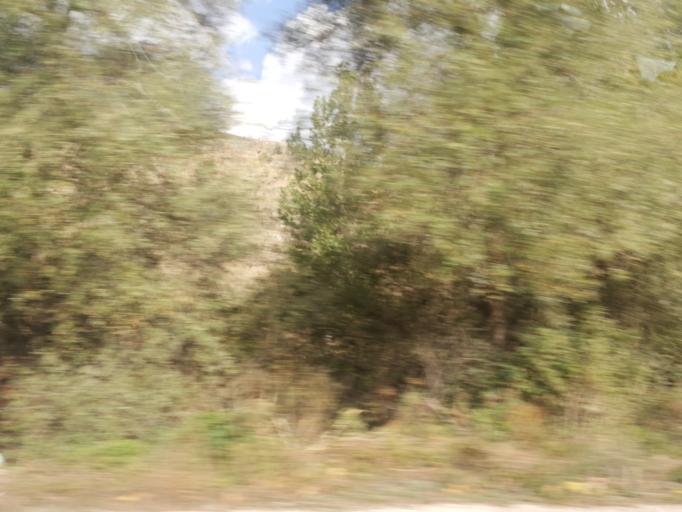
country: TR
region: Tokat
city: Artova
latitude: 40.0915
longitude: 36.3020
